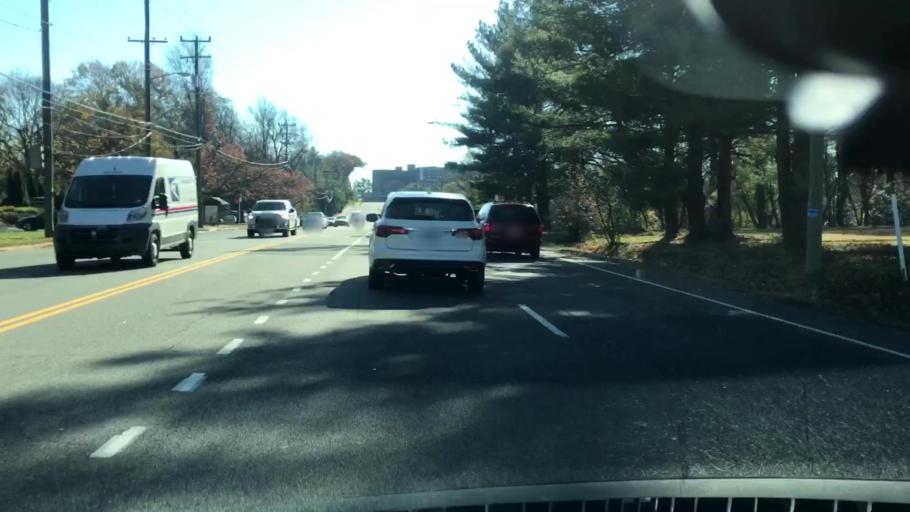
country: US
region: Virginia
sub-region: Fairfax County
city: Seven Corners
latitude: 38.8636
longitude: -77.1492
